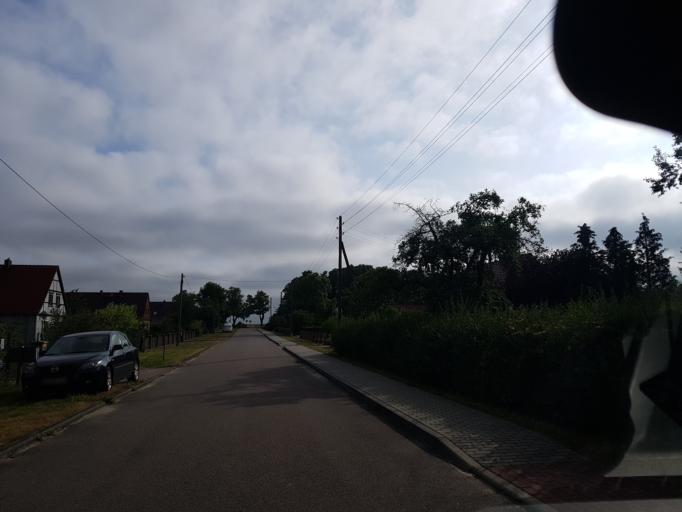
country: DE
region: Brandenburg
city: Juterbog
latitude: 51.9332
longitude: 13.1188
